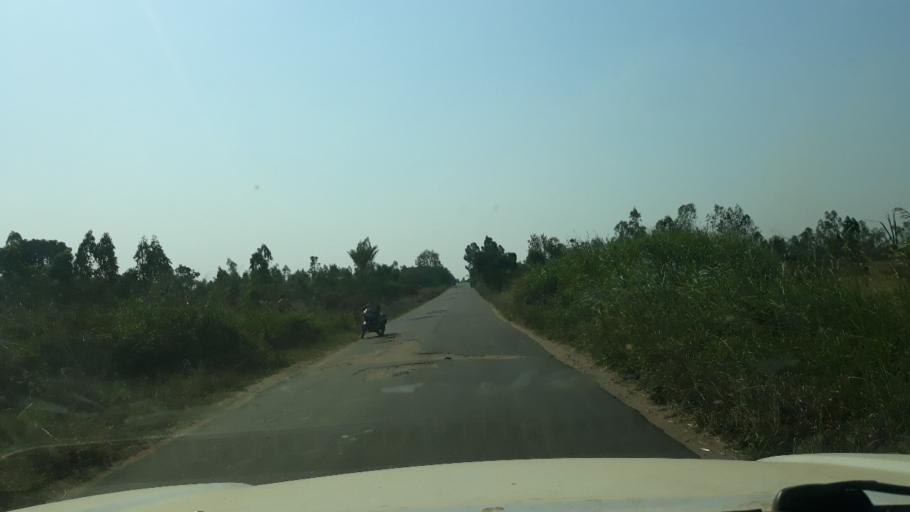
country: BI
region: Cibitoke
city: Cibitoke
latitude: -2.9685
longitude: 29.0842
